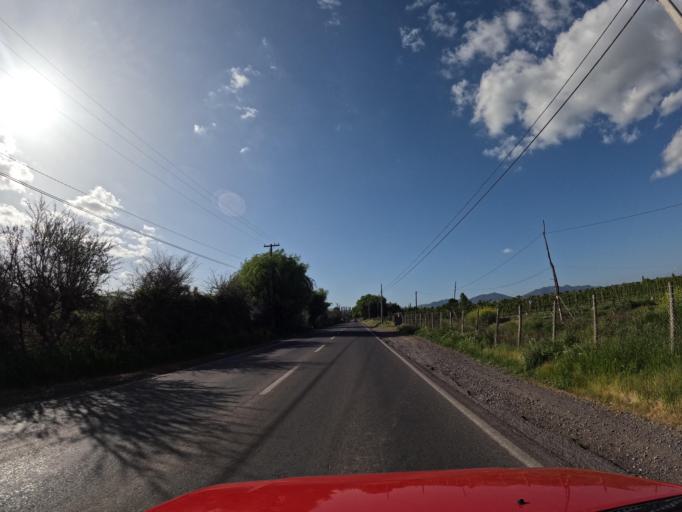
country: CL
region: Maule
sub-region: Provincia de Curico
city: Rauco
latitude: -34.9107
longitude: -71.2782
